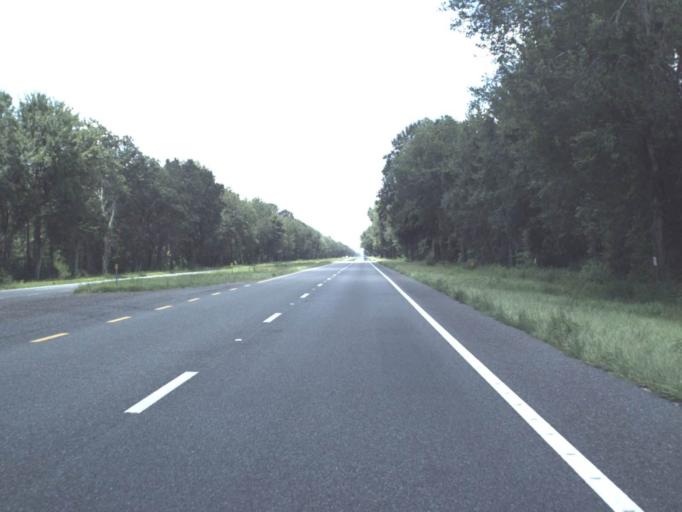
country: US
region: Florida
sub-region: Taylor County
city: Perry
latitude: 30.2228
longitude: -83.6751
